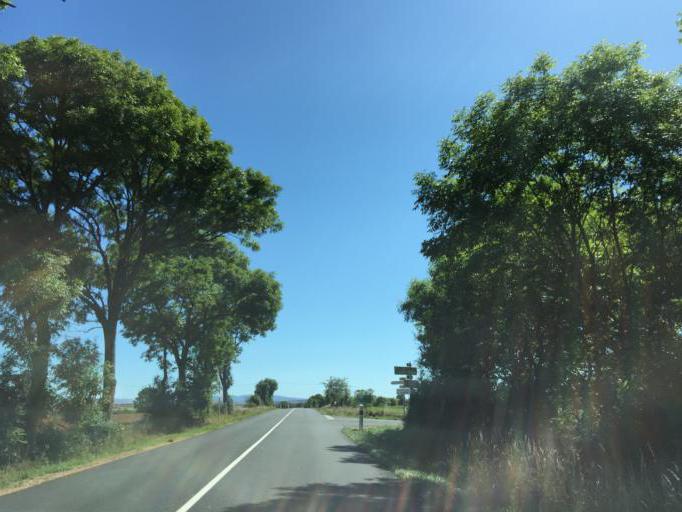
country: FR
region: Midi-Pyrenees
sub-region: Departement de l'Aveyron
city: La Cavalerie
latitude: 44.0151
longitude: 3.1123
